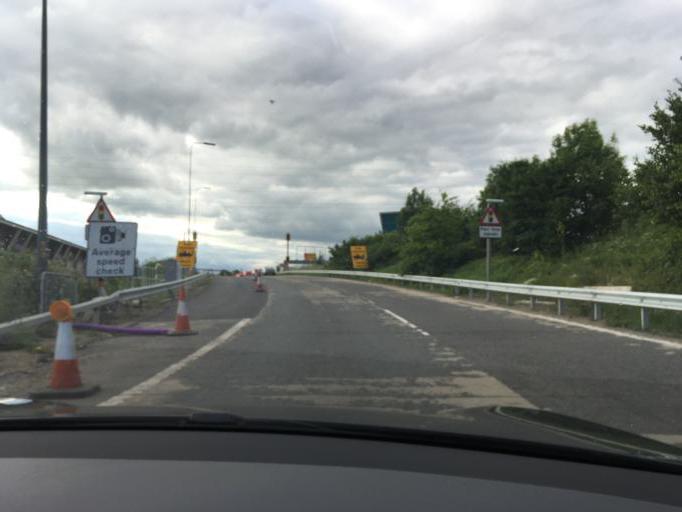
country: GB
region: England
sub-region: Trafford
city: Urmston
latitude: 53.4642
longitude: -2.3580
